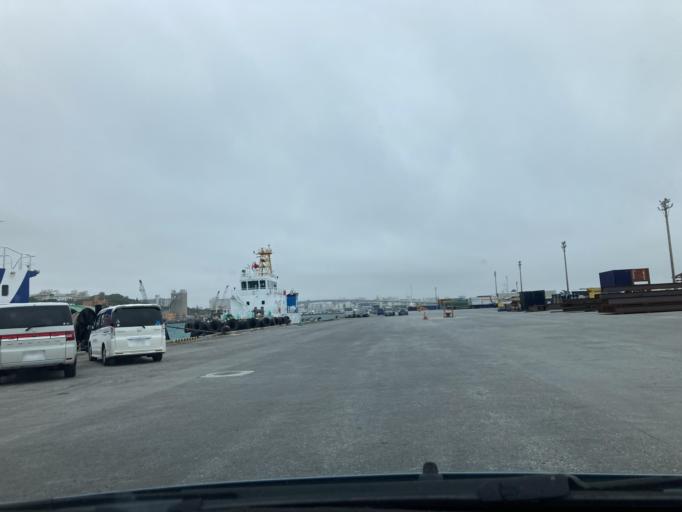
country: JP
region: Okinawa
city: Naha-shi
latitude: 26.2393
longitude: 127.6779
